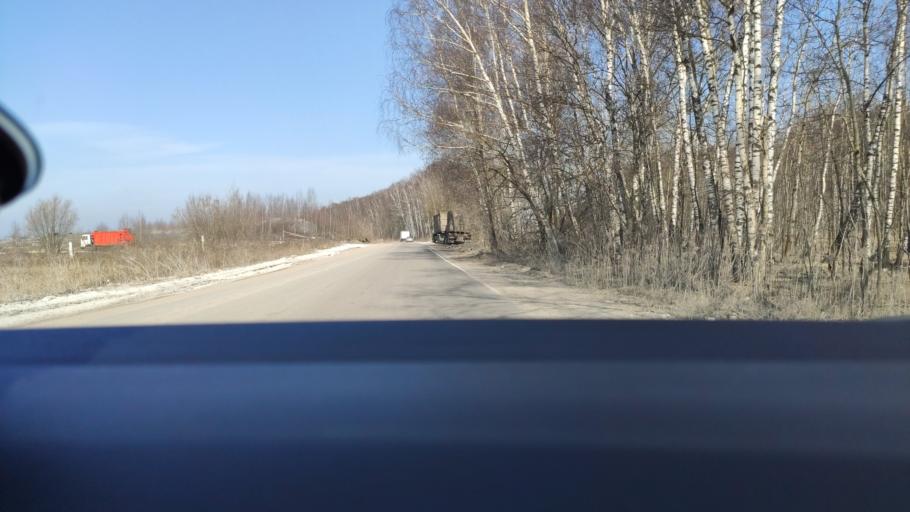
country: RU
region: Moskovskaya
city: Elektrostal'
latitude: 55.7667
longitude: 38.3863
